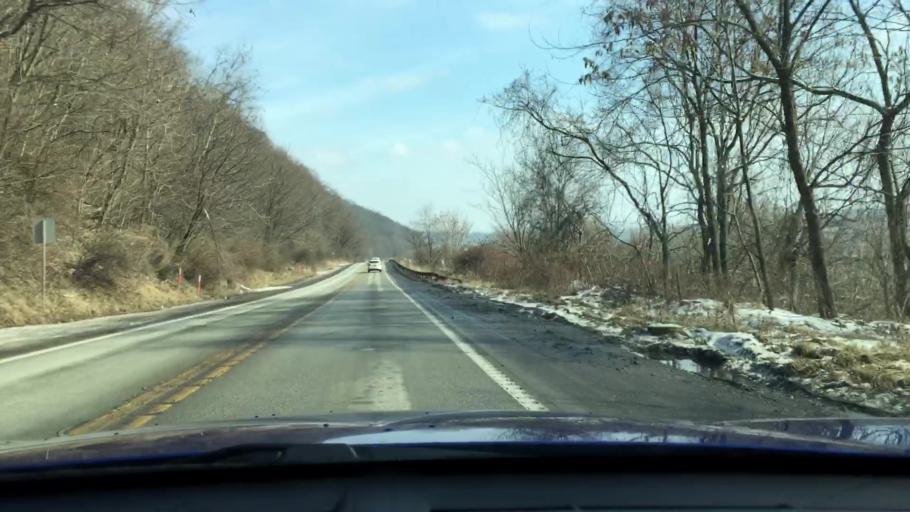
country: US
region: Pennsylvania
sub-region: Allegheny County
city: West Mifflin
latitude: 40.3561
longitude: -79.8757
